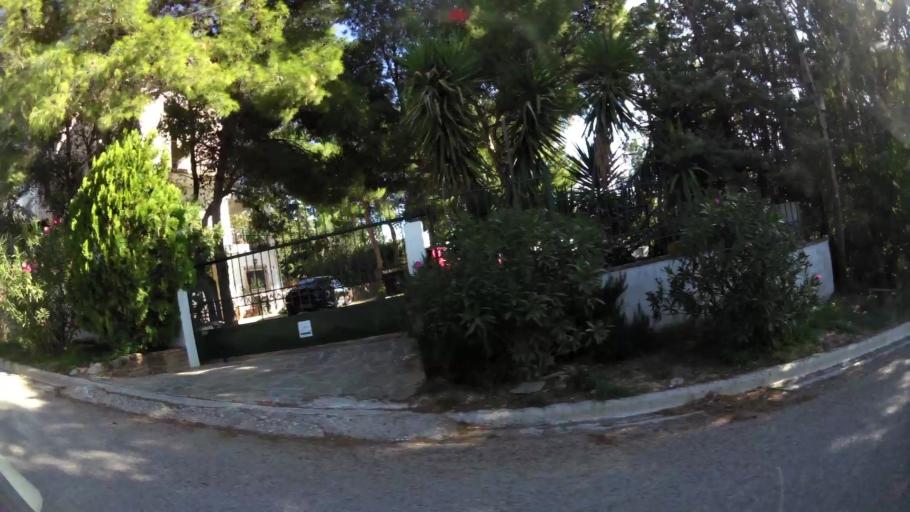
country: GR
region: Attica
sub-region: Nomarchia Anatolikis Attikis
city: Dhrafi
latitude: 38.0167
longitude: 23.8970
